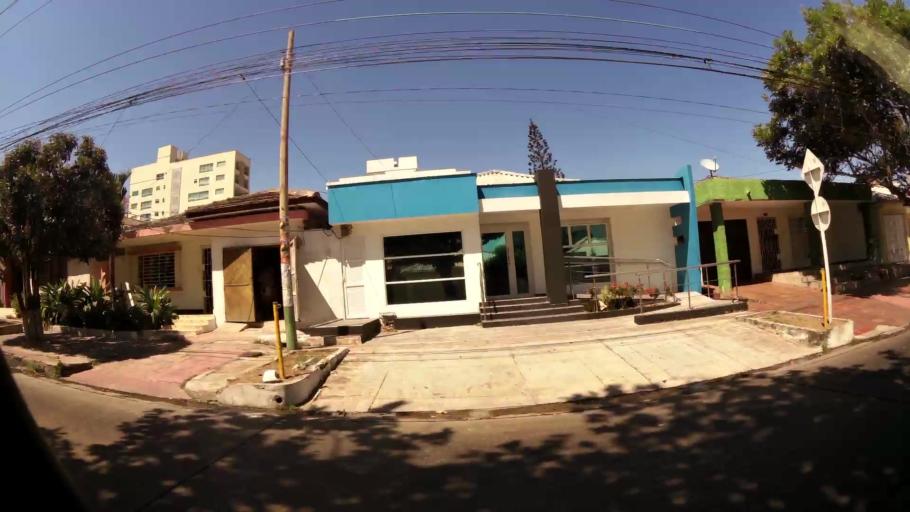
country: CO
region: Atlantico
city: Barranquilla
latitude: 10.9988
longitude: -74.8145
